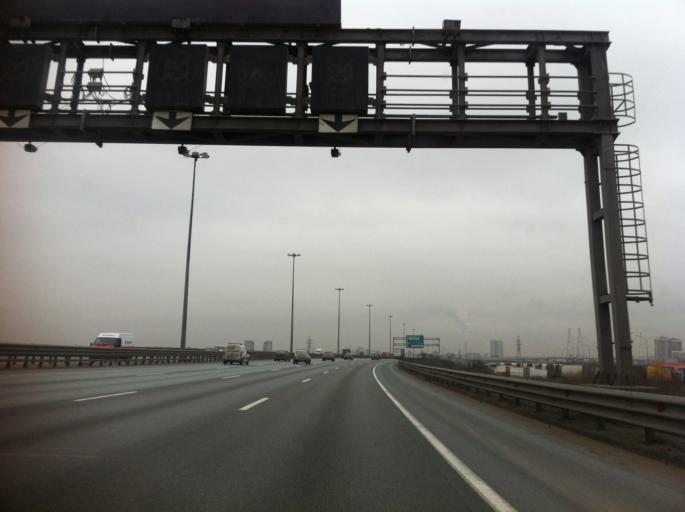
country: RU
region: Leningrad
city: Rybatskoye
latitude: 59.8659
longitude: 30.5281
